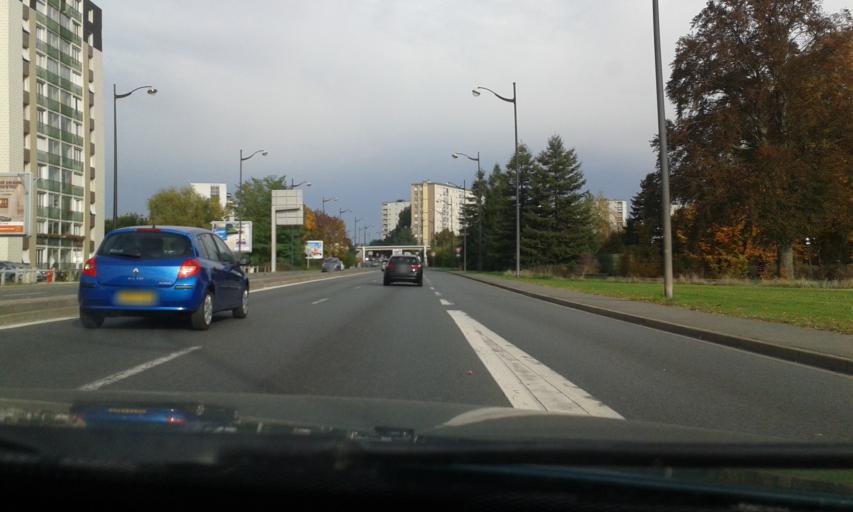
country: FR
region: Centre
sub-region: Departement du Loiret
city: Orleans
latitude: 47.8902
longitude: 1.8954
